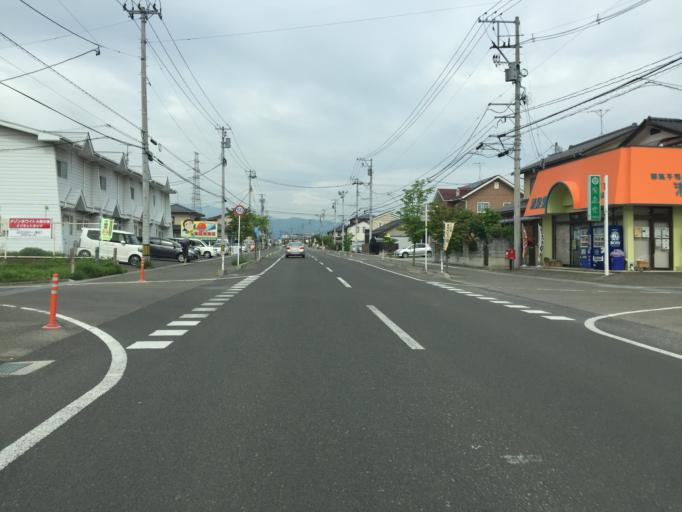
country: JP
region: Fukushima
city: Fukushima-shi
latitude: 37.7854
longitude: 140.4475
